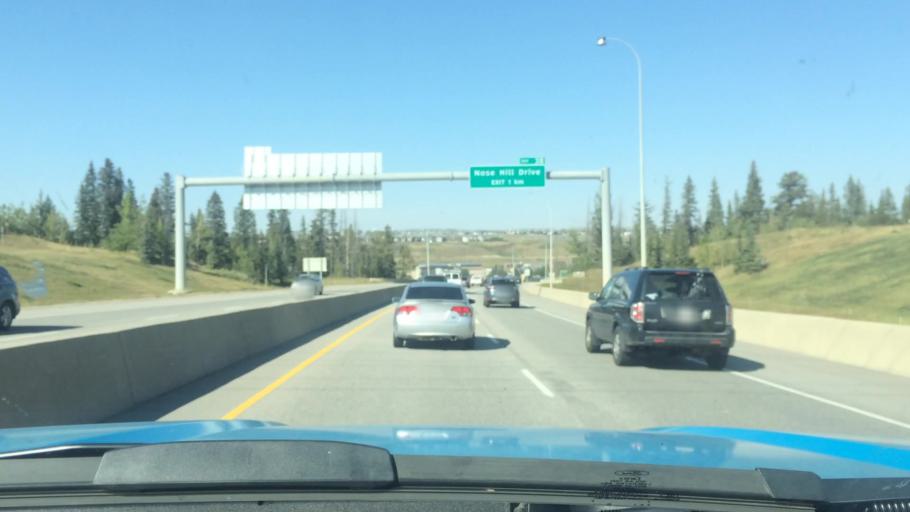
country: CA
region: Alberta
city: Calgary
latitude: 51.0948
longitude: -114.2334
